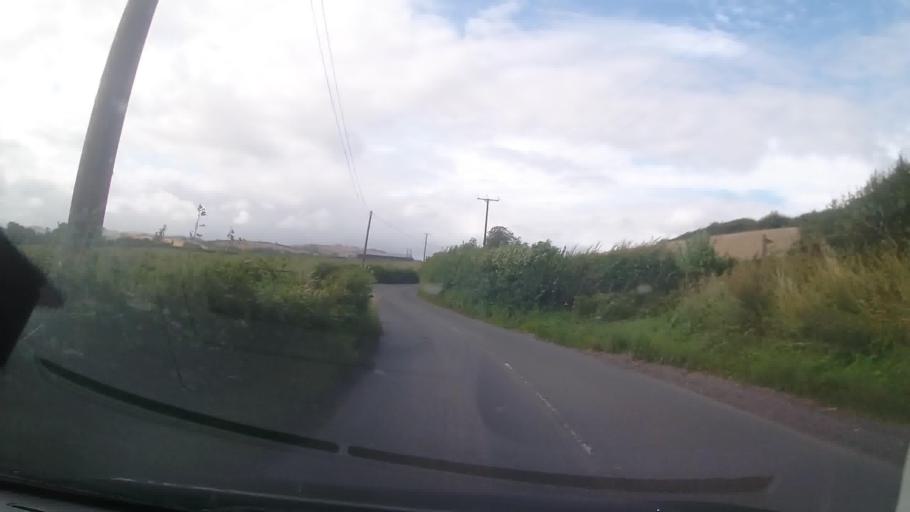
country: GB
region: England
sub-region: Shropshire
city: Acton
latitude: 52.4276
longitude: -3.0326
